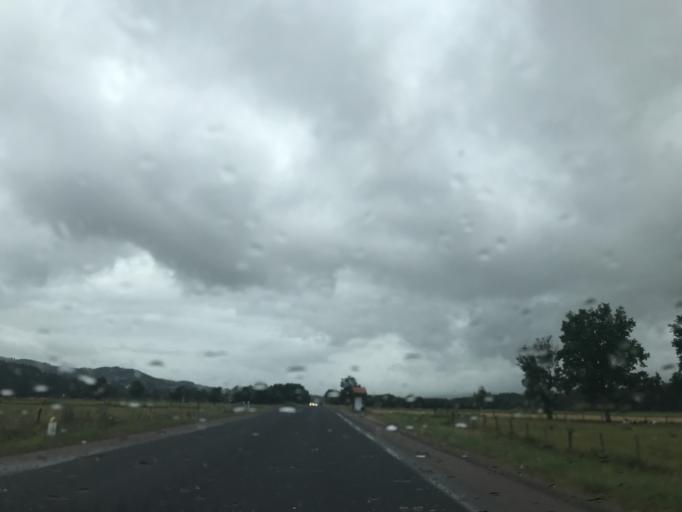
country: FR
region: Auvergne
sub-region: Departement du Puy-de-Dome
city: Marsac-en-Livradois
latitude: 45.5125
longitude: 3.7273
